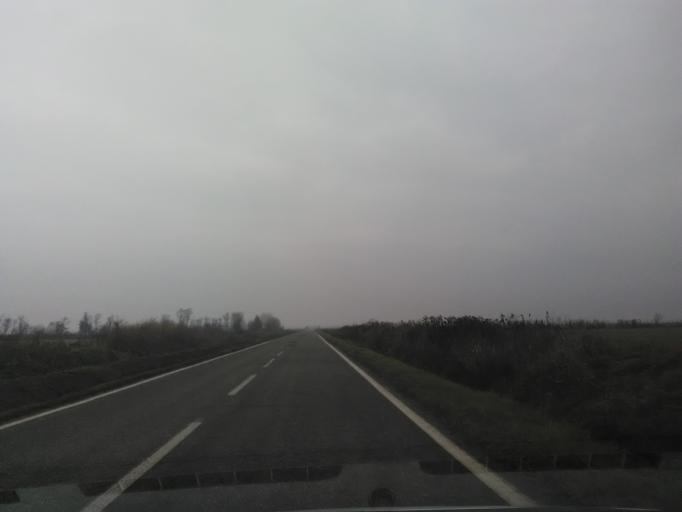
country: IT
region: Piedmont
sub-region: Provincia di Vercelli
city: Salasco
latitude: 45.3070
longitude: 8.2521
